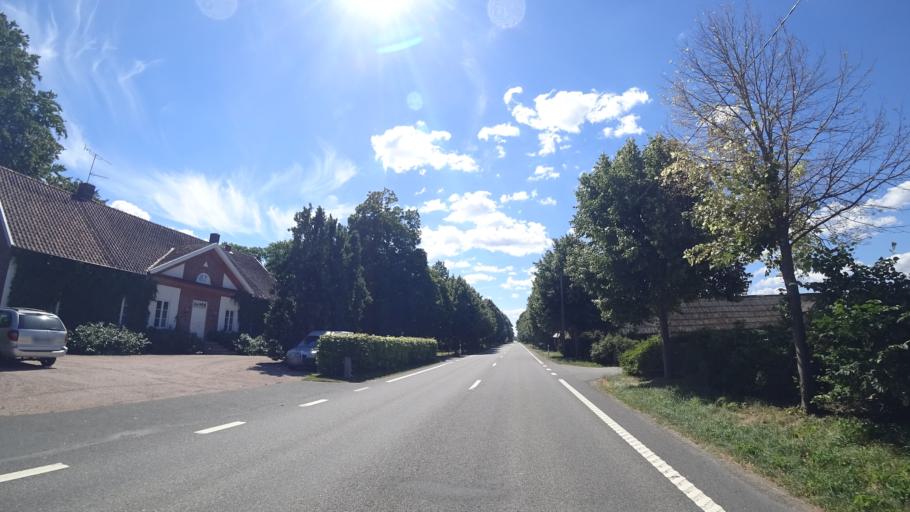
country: SE
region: Skane
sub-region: Kristianstads Kommun
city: Onnestad
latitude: 56.0700
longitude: 14.0839
